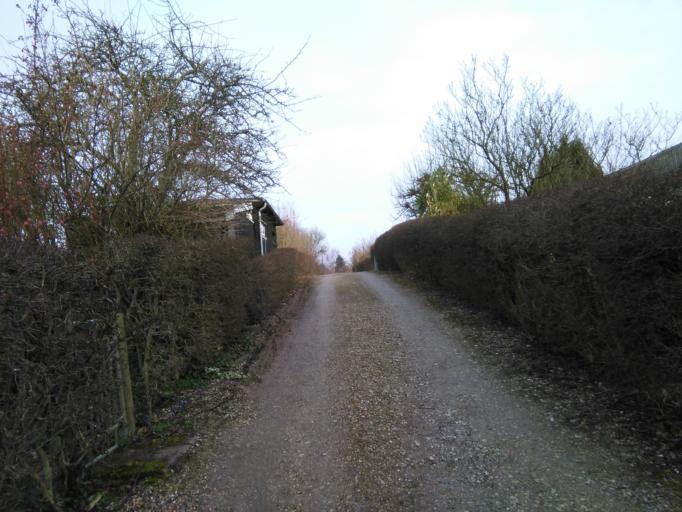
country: DK
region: Central Jutland
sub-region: Arhus Kommune
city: Arhus
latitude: 56.1226
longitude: 10.2030
